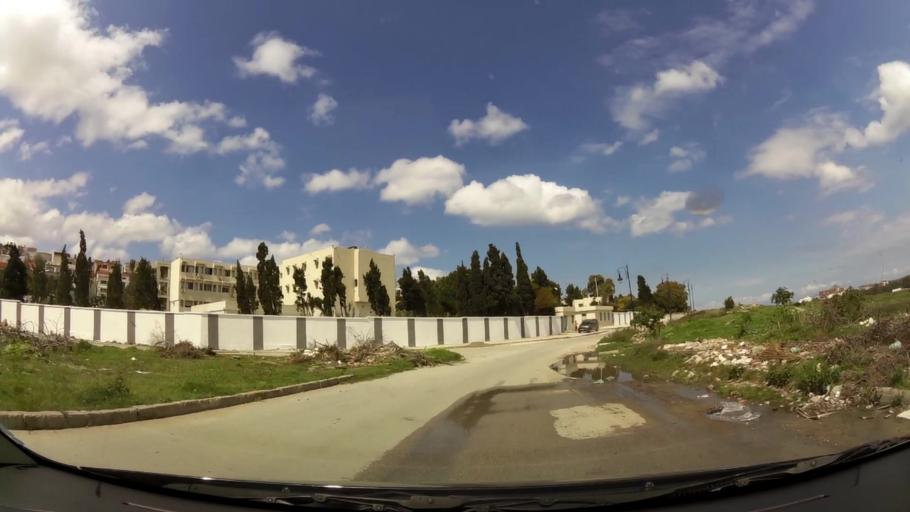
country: MA
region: Tanger-Tetouan
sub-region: Tanger-Assilah
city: Tangier
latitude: 35.7746
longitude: -5.7691
